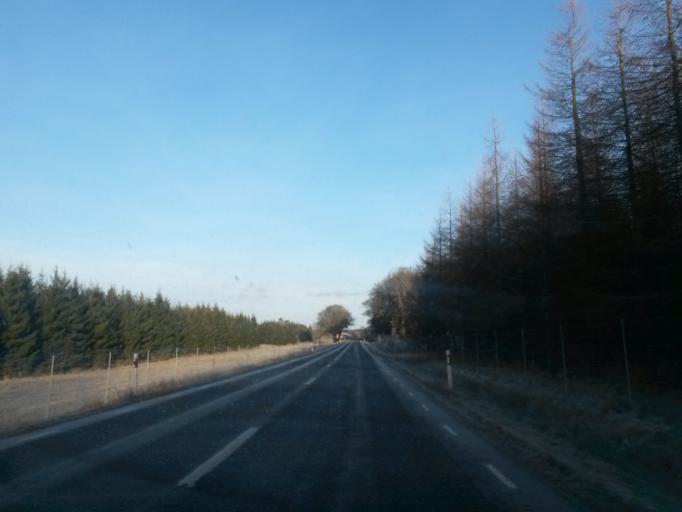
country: SE
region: Vaestra Goetaland
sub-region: Alingsas Kommun
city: Sollebrunn
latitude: 58.1529
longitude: 12.4194
